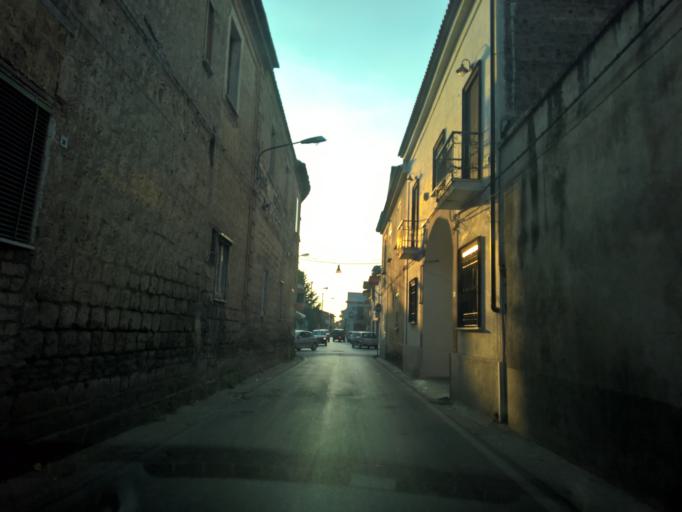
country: IT
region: Campania
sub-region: Provincia di Caserta
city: San Prisco
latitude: 41.0879
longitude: 14.2801
